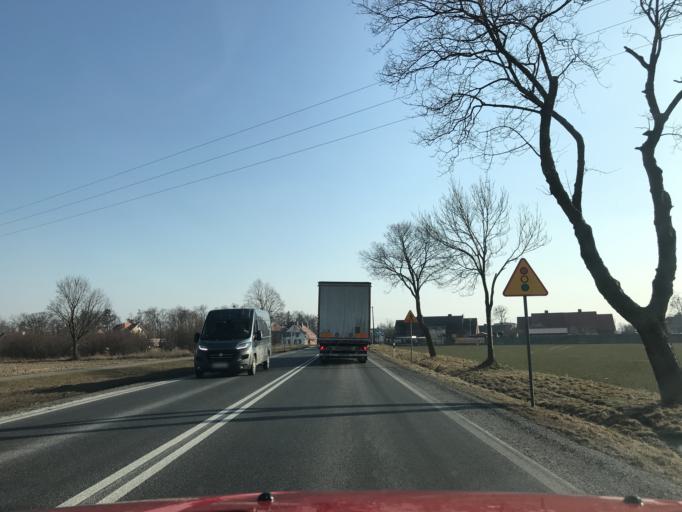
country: PL
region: Greater Poland Voivodeship
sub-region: Powiat sredzki
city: Nowe Miasto nad Warta
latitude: 52.0773
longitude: 17.4179
